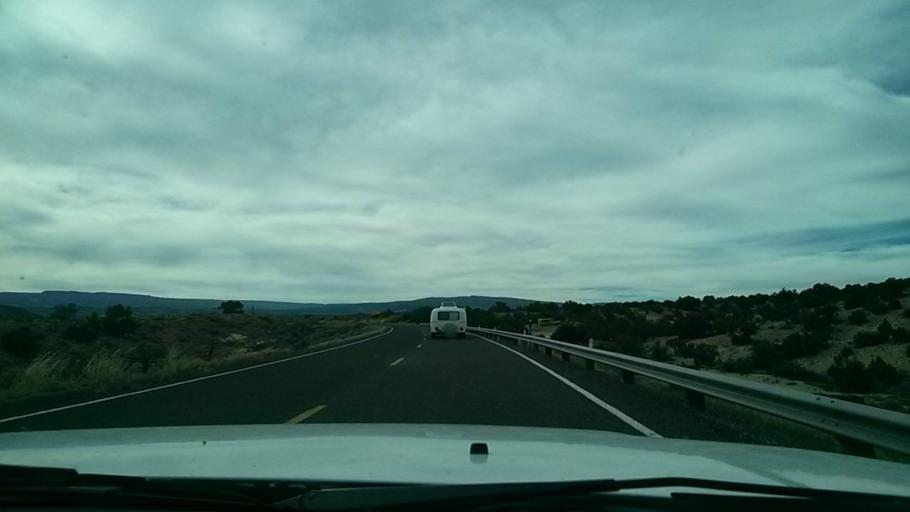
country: US
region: Utah
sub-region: Wayne County
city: Loa
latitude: 37.7557
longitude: -111.5702
